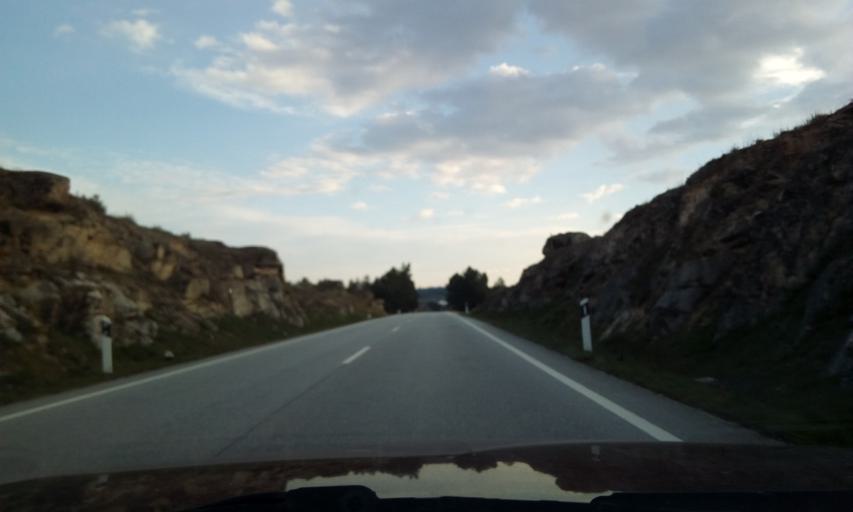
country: PT
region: Guarda
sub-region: Pinhel
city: Pinhel
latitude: 40.6803
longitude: -6.9504
